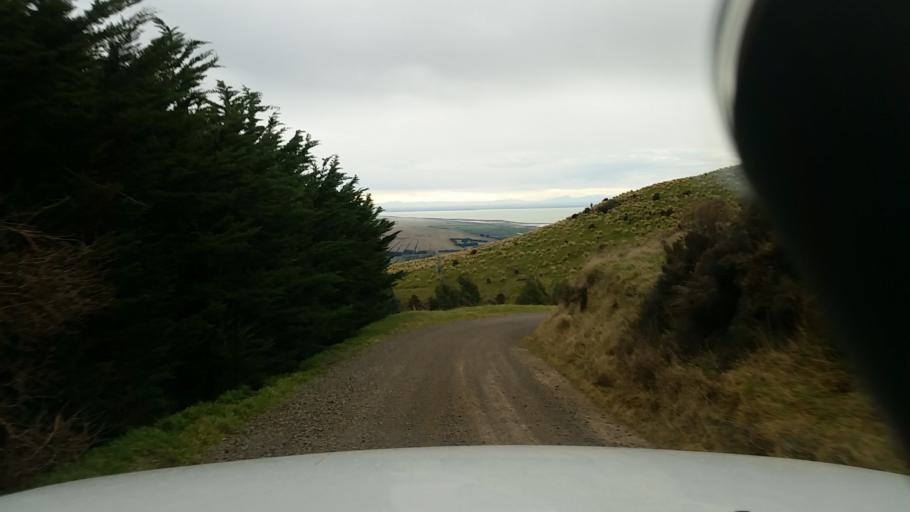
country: NZ
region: Canterbury
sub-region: Christchurch City
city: Christchurch
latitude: -43.8164
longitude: 172.7519
